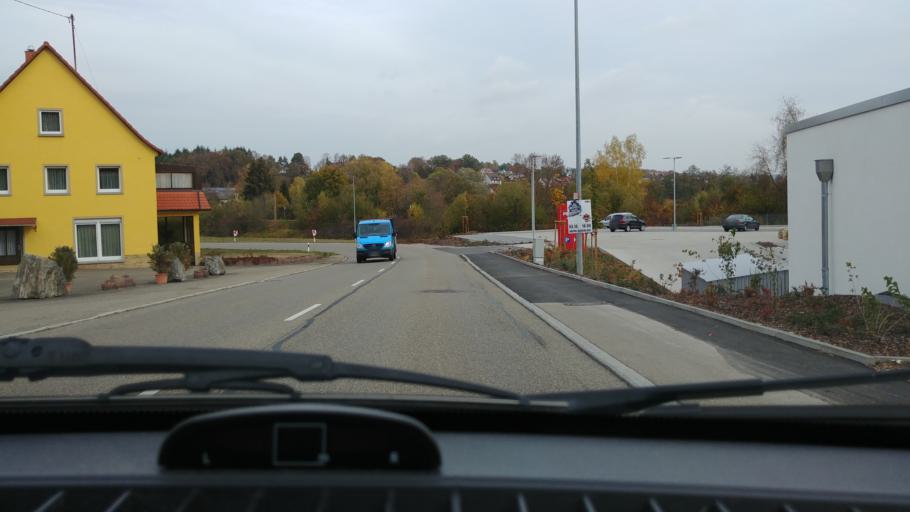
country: DE
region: Baden-Wuerttemberg
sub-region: Regierungsbezirk Stuttgart
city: Stimpfach
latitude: 49.0578
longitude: 10.0812
